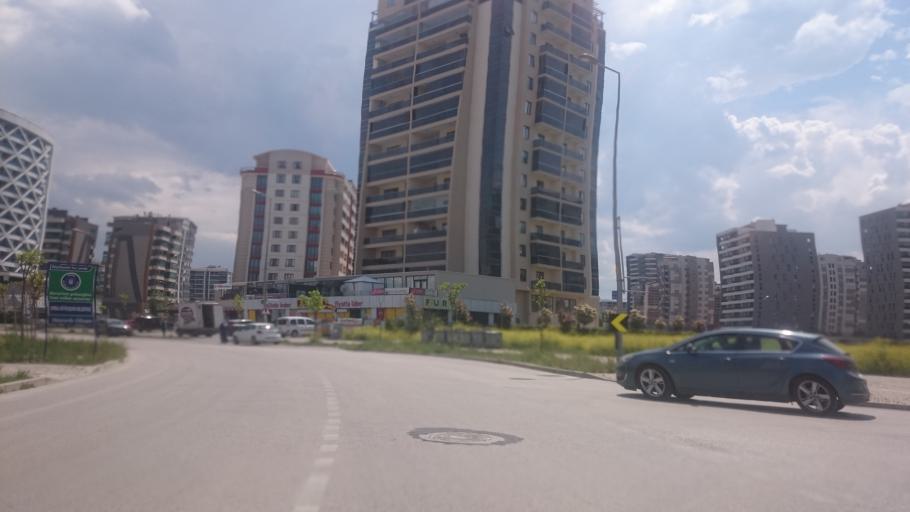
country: TR
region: Bursa
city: Cali
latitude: 40.2205
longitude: 28.9445
